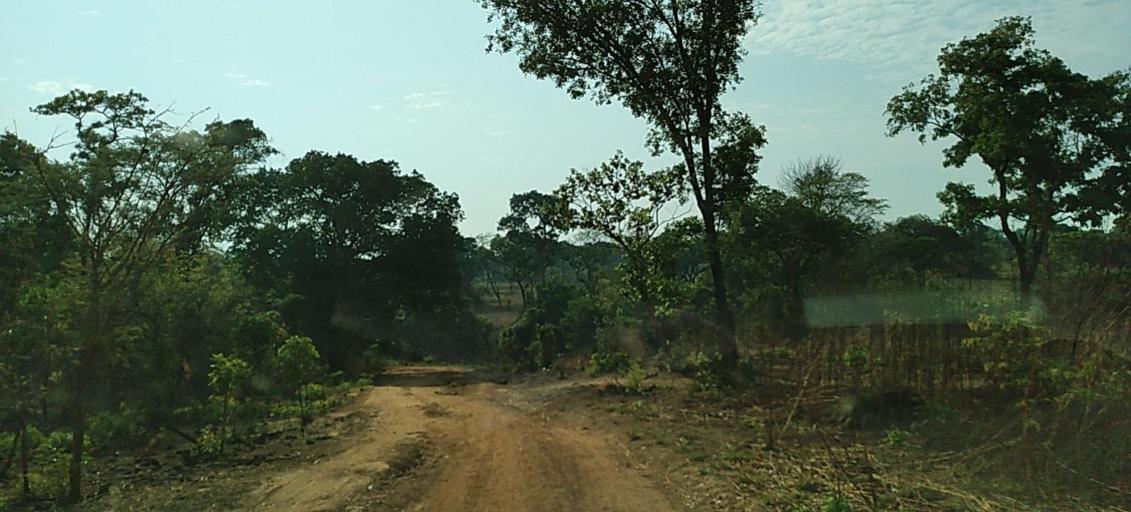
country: ZM
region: Copperbelt
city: Kalulushi
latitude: -13.0070
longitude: 27.7188
